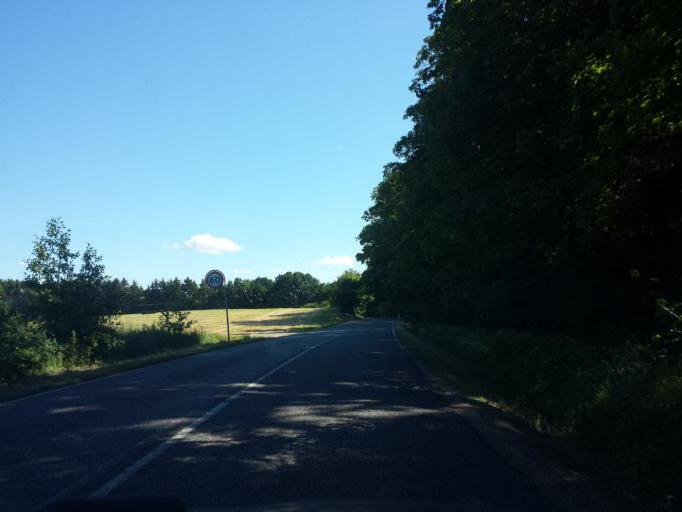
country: DK
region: Capital Region
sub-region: Egedal Kommune
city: Ganlose
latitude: 55.8079
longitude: 12.2619
